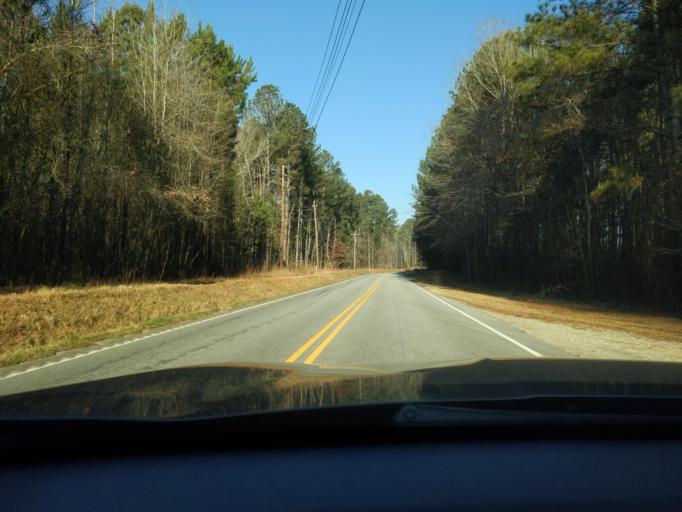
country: US
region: South Carolina
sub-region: Greenwood County
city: Ninety Six
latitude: 34.1770
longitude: -82.0939
